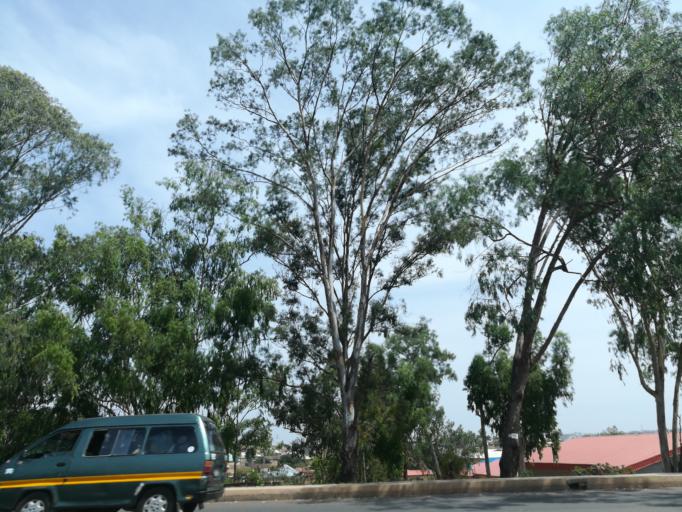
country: NG
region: Plateau
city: Bukuru
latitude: 9.8413
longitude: 8.8660
